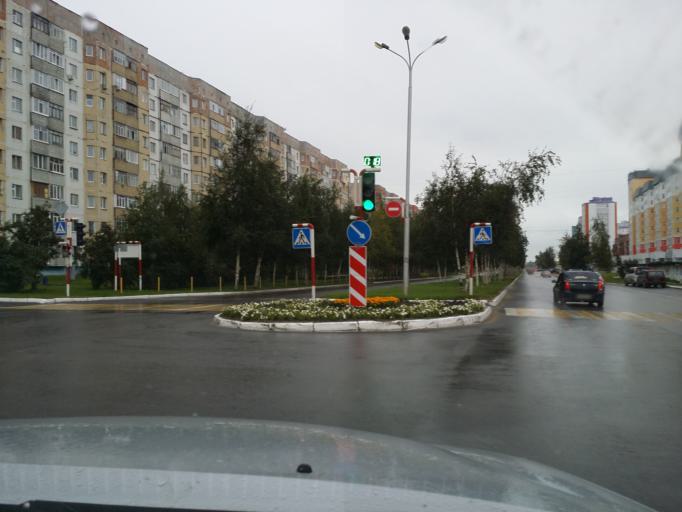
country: RU
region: Khanty-Mansiyskiy Avtonomnyy Okrug
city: Nizhnevartovsk
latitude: 60.9325
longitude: 76.5881
